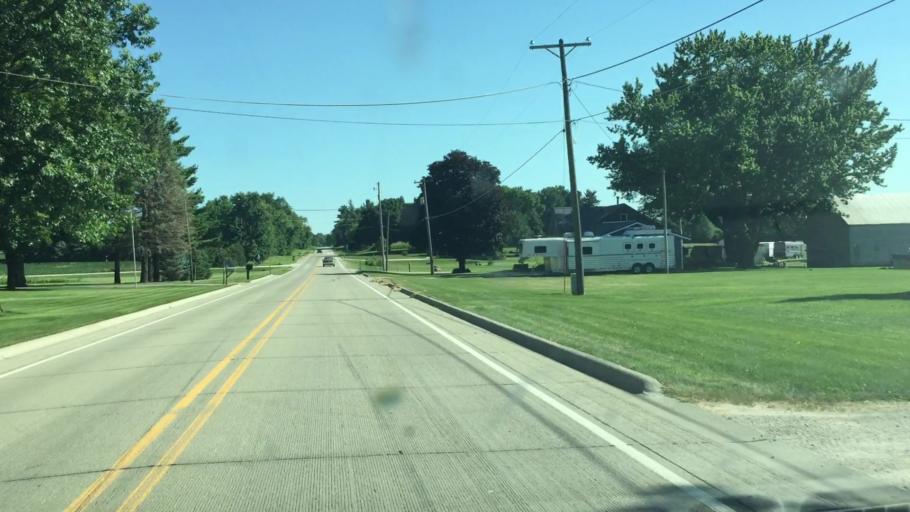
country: US
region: Iowa
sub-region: Linn County
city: Ely
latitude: 41.8637
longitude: -91.6464
